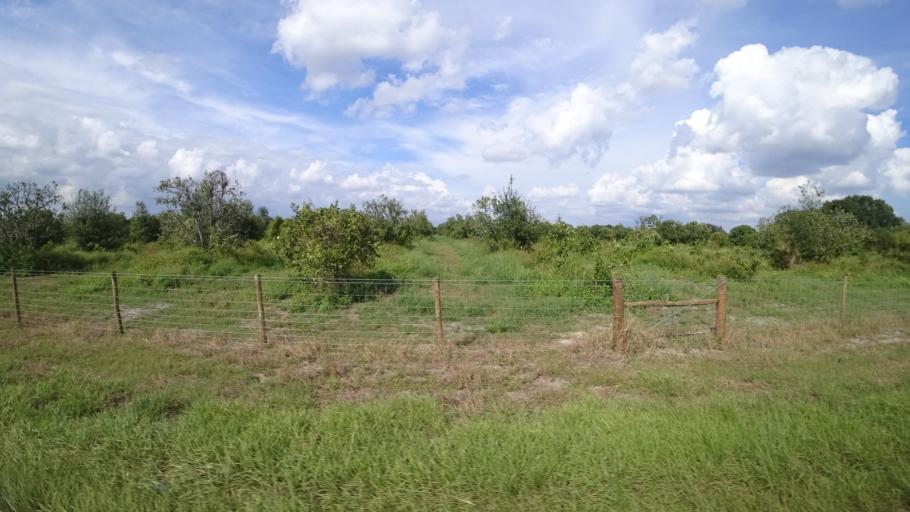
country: US
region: Florida
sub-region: Hillsborough County
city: Wimauma
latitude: 27.5373
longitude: -82.0905
